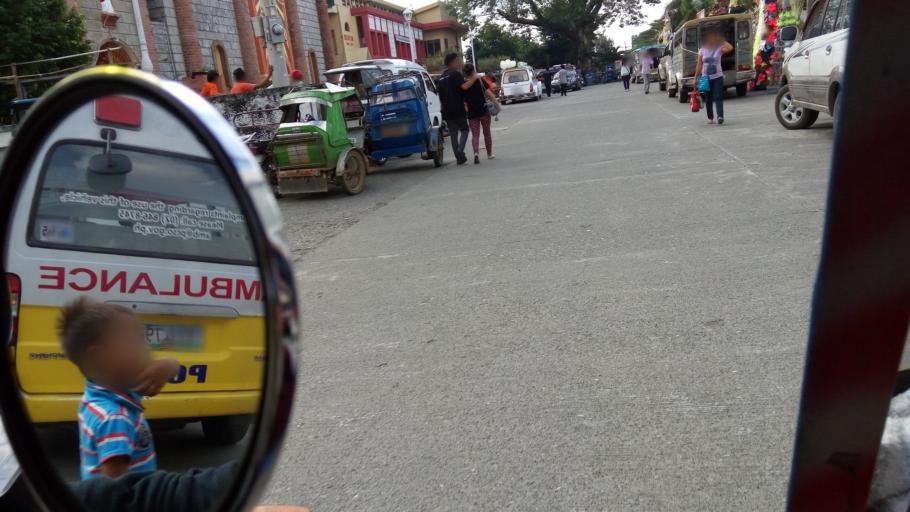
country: PH
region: Ilocos
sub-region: Province of La Union
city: Bauang
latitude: 16.5265
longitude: 120.3306
